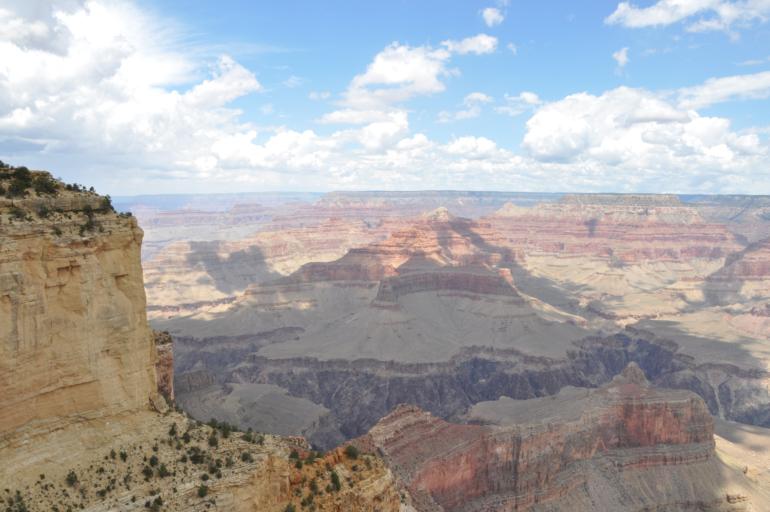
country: US
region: Arizona
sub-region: Coconino County
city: Grand Canyon
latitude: 36.0721
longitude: -112.1482
